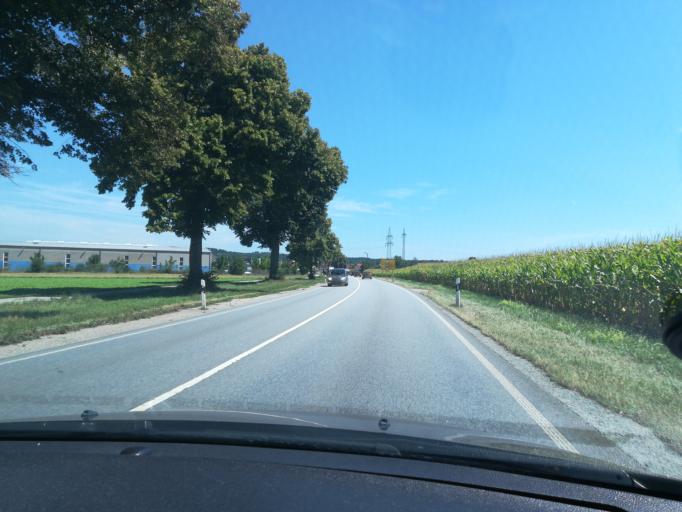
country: DE
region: Bavaria
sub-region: Upper Bavaria
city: Hohenlinden
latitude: 48.1551
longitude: 11.9833
